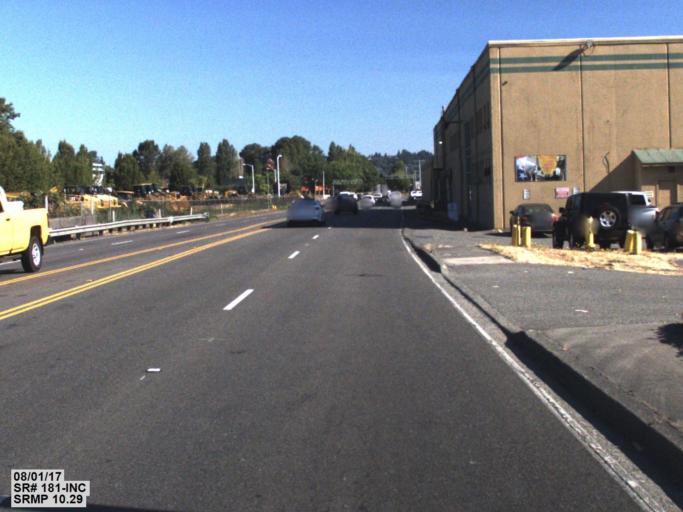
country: US
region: Washington
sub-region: King County
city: Tukwila
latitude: 47.4484
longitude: -122.2433
